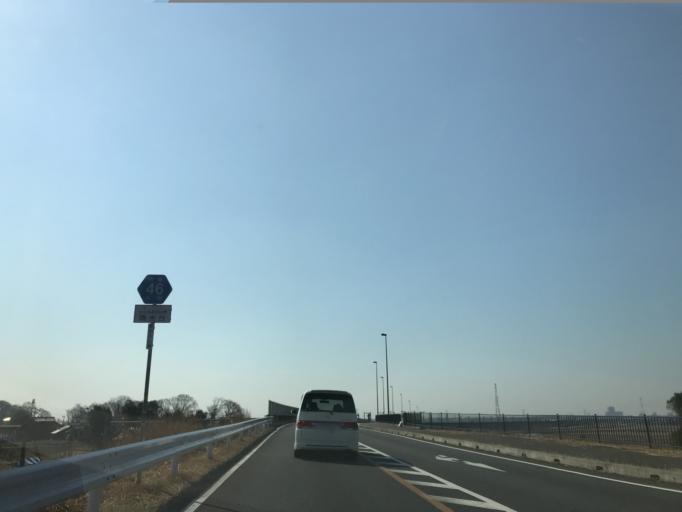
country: JP
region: Ibaraki
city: Mitsukaido
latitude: 35.9915
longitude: 140.0361
